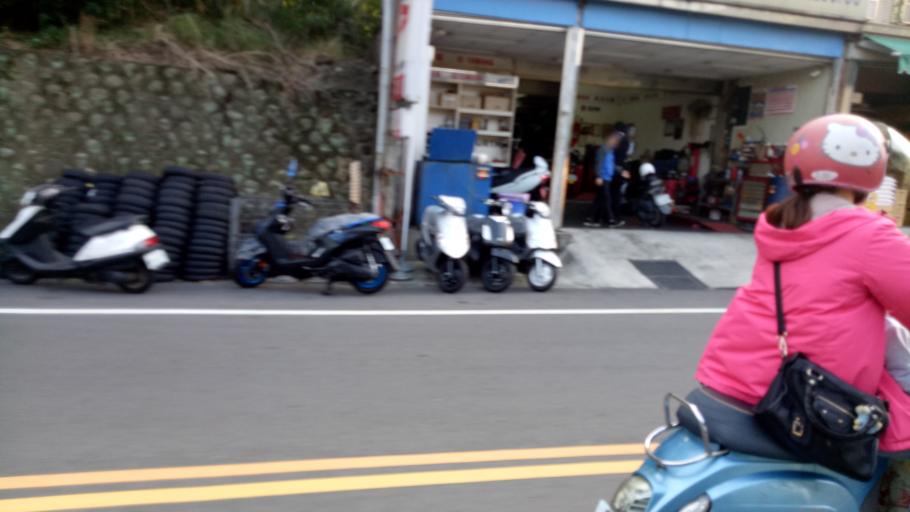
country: TW
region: Taiwan
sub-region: Hsinchu
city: Hsinchu
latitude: 24.7674
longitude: 120.9802
